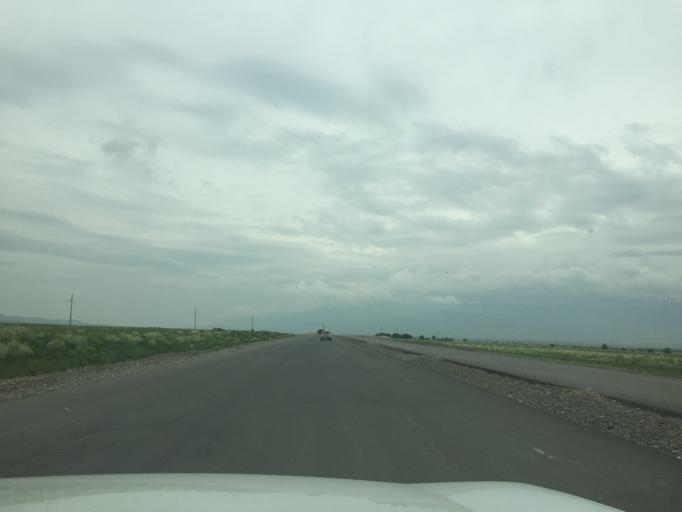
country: KZ
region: Ongtustik Qazaqstan
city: Turar Ryskulov
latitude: 42.5098
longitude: 70.3961
